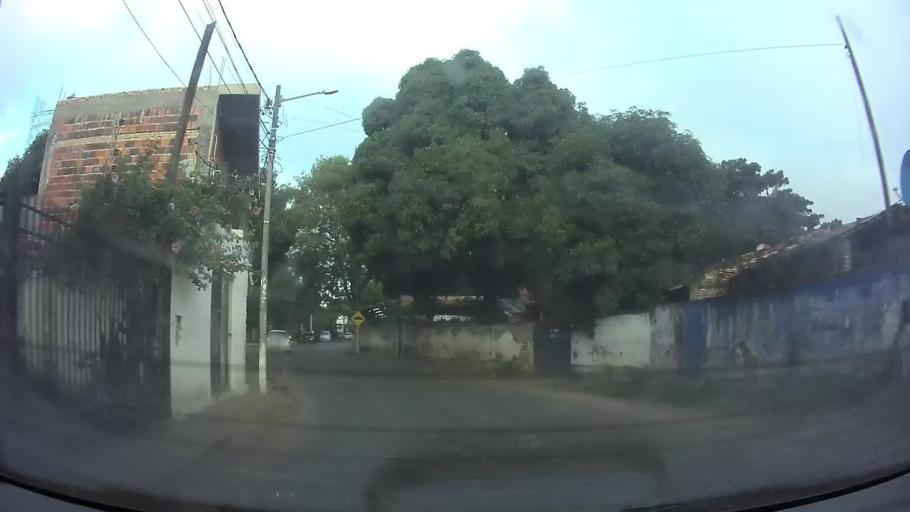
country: PY
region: Central
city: Lambare
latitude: -25.3319
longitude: -57.5718
